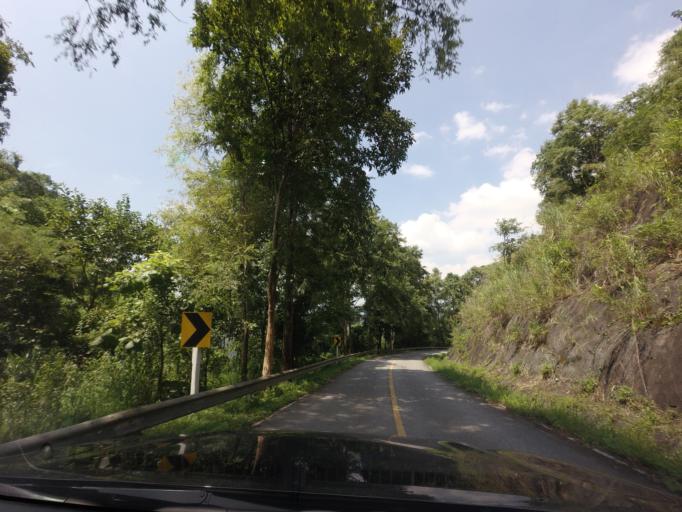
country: TH
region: Loei
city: Na Haeo
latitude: 17.6291
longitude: 100.9031
